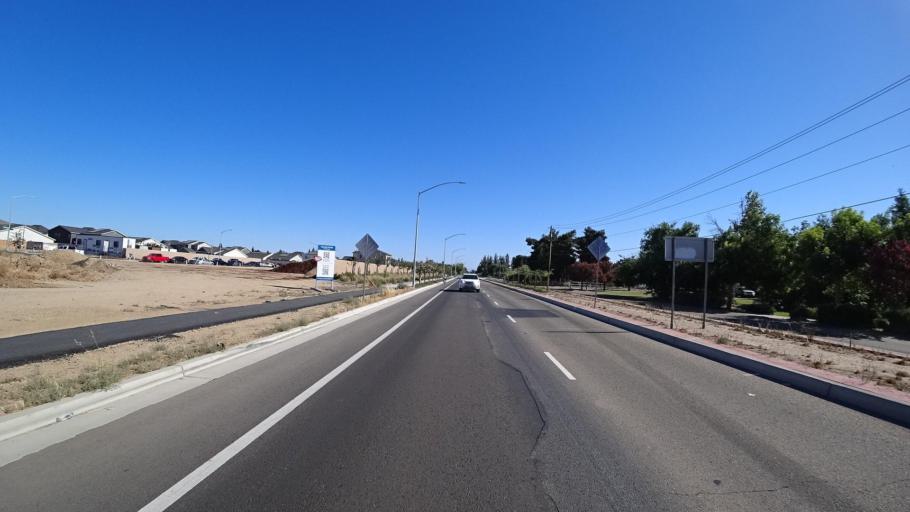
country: US
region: California
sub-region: Fresno County
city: Sunnyside
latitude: 36.7165
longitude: -119.6822
